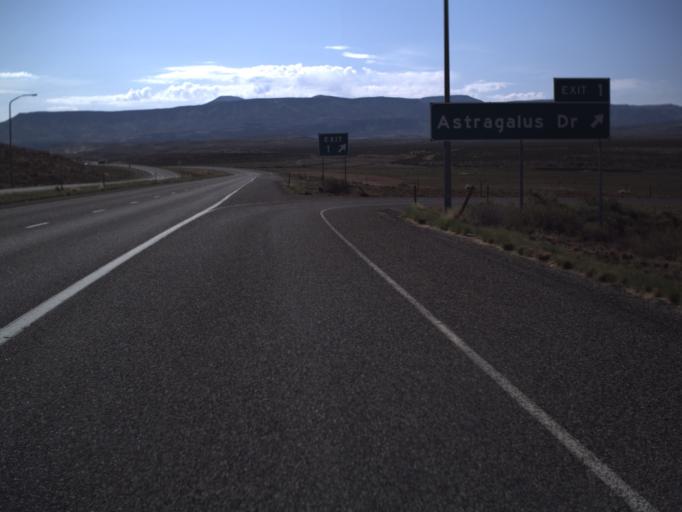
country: US
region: Utah
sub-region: Washington County
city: Saint George
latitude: 37.0239
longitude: -113.6012
